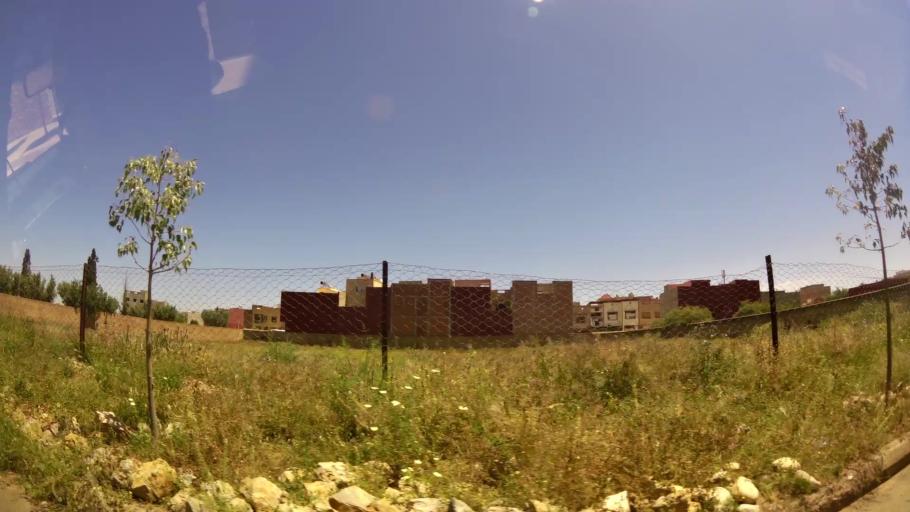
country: MA
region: Oriental
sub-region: Oujda-Angad
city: Oujda
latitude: 34.6703
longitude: -1.8709
